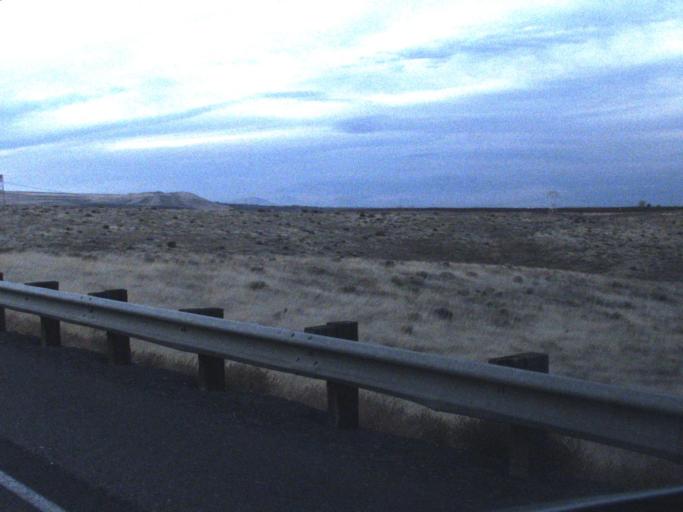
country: US
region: Washington
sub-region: Benton County
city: Finley
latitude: 46.0527
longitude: -118.8770
